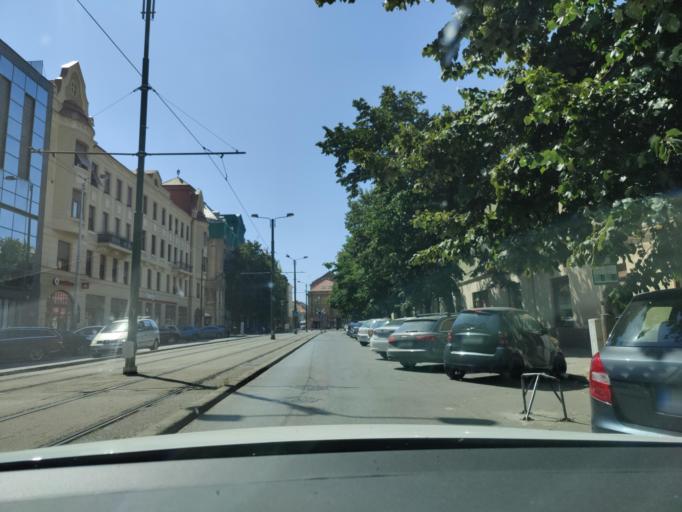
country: RO
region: Timis
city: Timisoara
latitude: 45.7557
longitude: 21.2310
